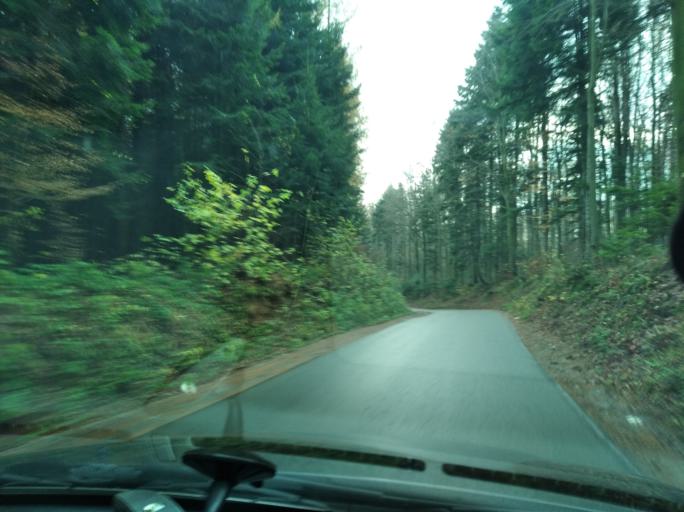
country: PL
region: Subcarpathian Voivodeship
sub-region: Powiat strzyzowski
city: Strzyzow
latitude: 49.9031
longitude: 21.7846
